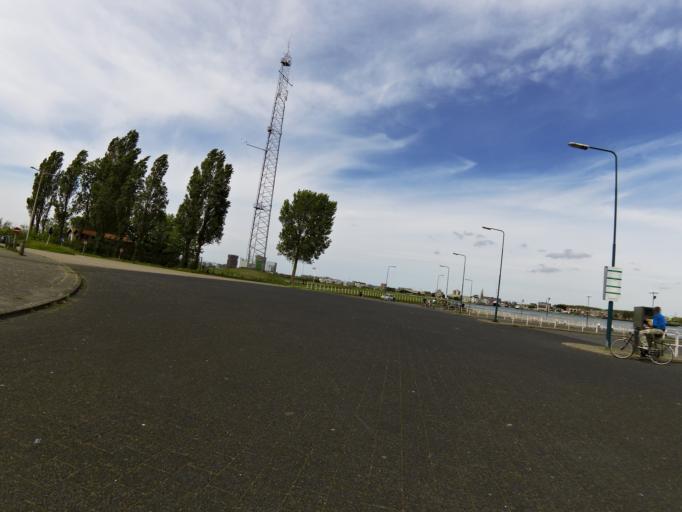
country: NL
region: South Holland
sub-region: Gemeente Maassluis
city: Maassluis
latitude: 51.9111
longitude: 4.2425
